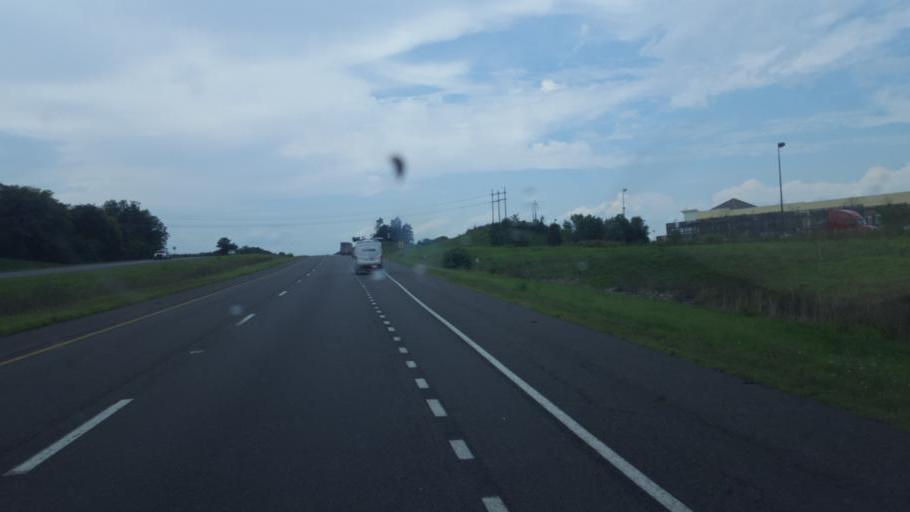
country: US
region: Virginia
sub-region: Warren County
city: Front Royal
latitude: 38.9580
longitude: -78.1880
